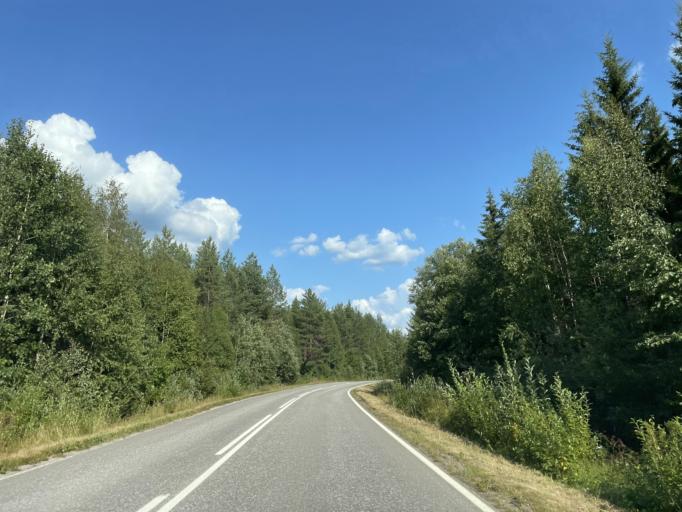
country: FI
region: Central Finland
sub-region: Saarijaervi-Viitasaari
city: Pihtipudas
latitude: 63.3658
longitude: 25.7050
